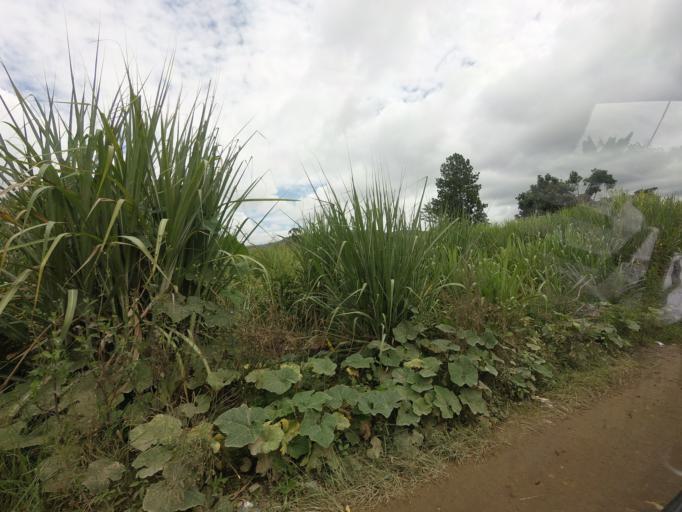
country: CO
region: Huila
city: Isnos
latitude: 1.9572
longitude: -76.2923
